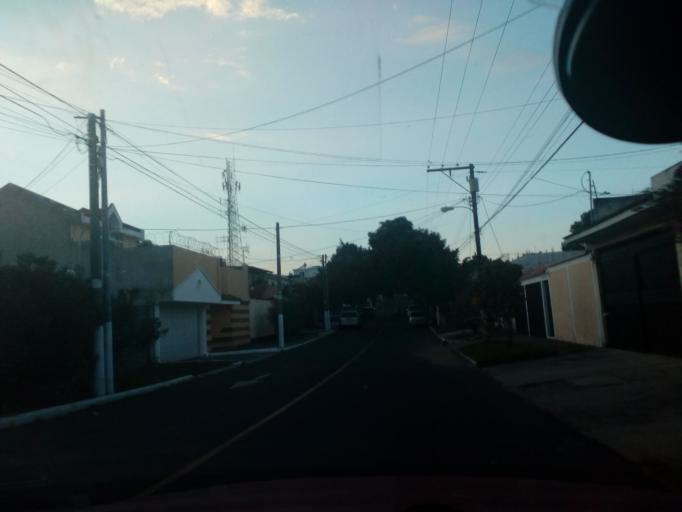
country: GT
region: Guatemala
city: Mixco
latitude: 14.6041
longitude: -90.5793
